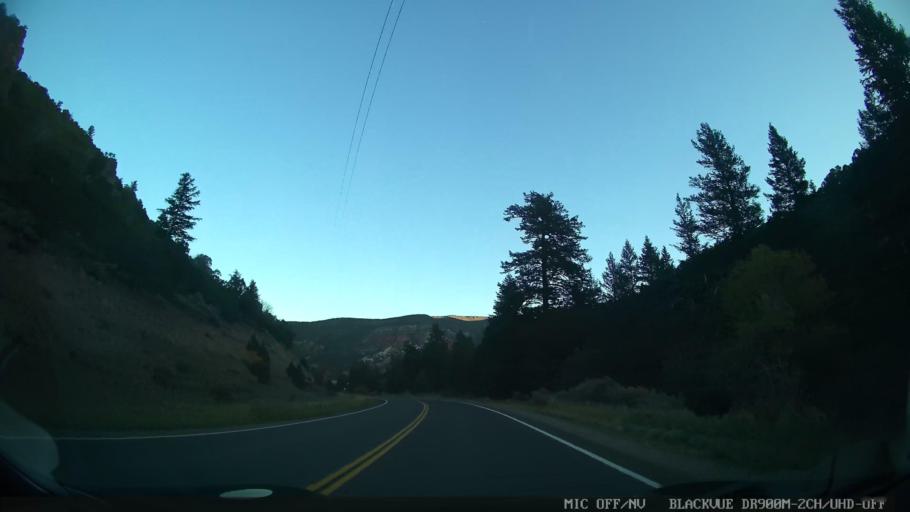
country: US
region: Colorado
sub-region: Eagle County
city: Edwards
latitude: 39.8501
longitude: -106.6439
